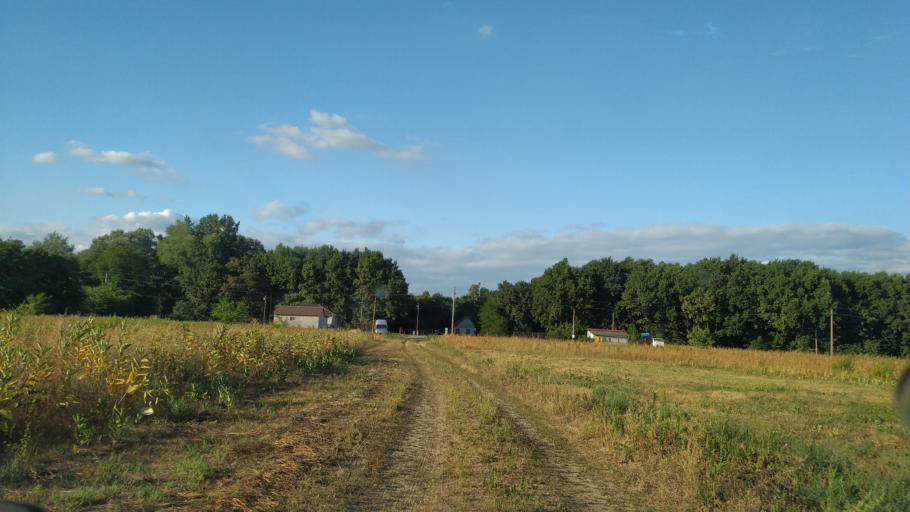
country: HU
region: Pest
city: Nagykata
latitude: 47.3996
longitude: 19.7430
